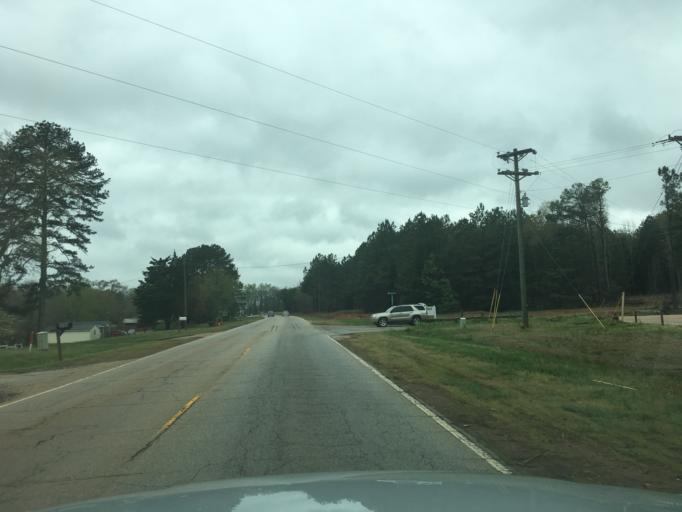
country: US
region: South Carolina
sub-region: Spartanburg County
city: Wellford
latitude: 34.9622
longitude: -82.0627
